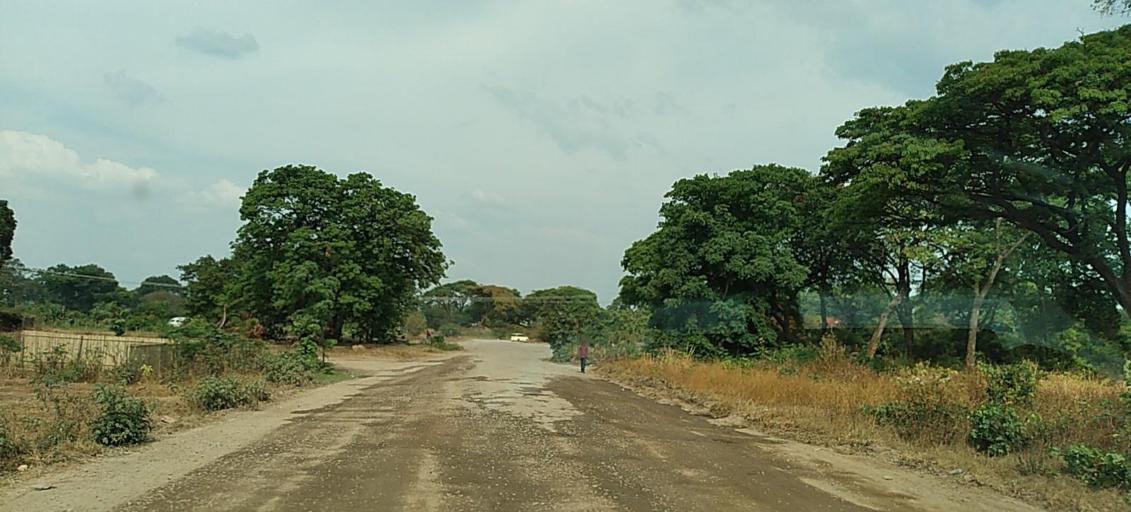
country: ZM
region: Copperbelt
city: Chililabombwe
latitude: -12.3733
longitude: 27.8259
